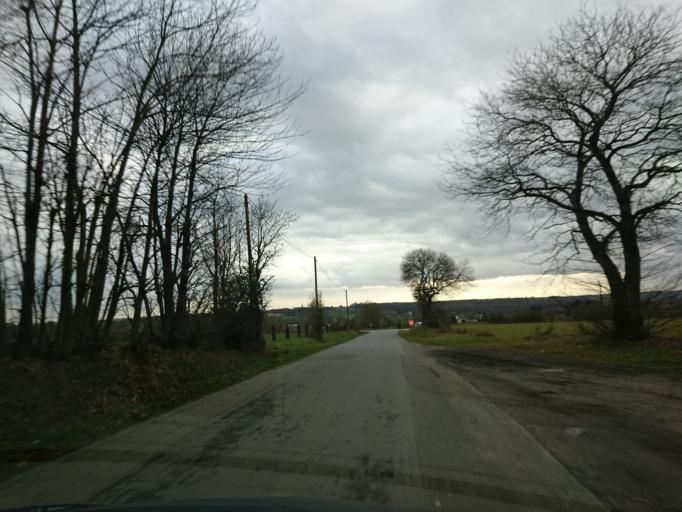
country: FR
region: Brittany
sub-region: Departement d'Ille-et-Vilaine
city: Pance
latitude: 47.9041
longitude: -1.6469
